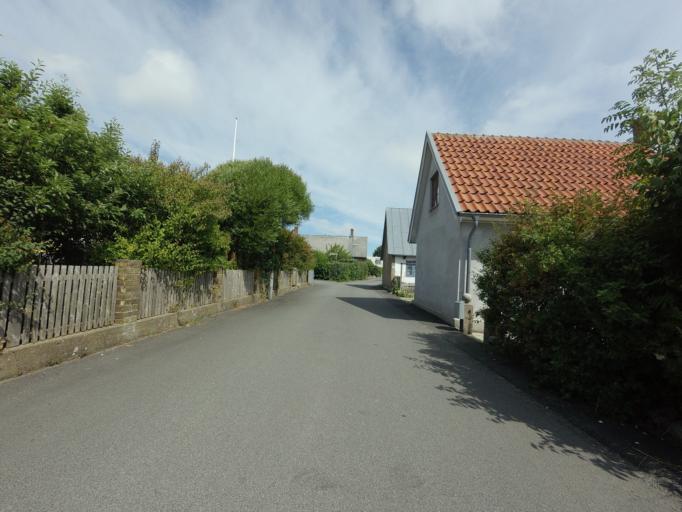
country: SE
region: Skane
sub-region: Simrishamns Kommun
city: Simrishamn
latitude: 55.5191
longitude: 14.3464
